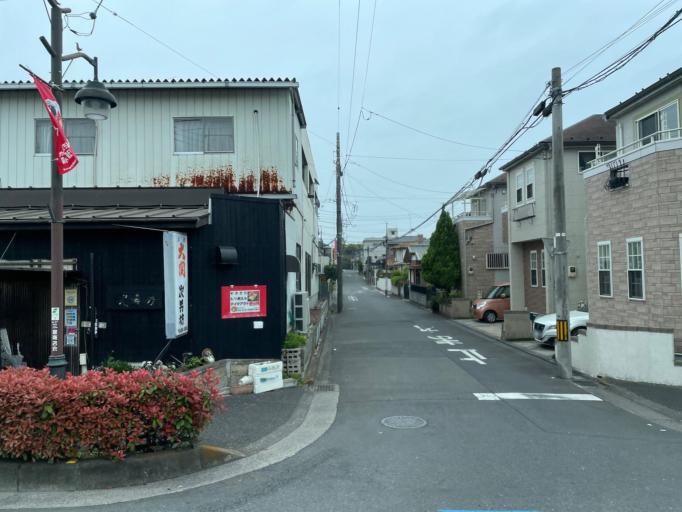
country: JP
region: Saitama
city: Saitama
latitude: 35.8875
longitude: 139.6911
